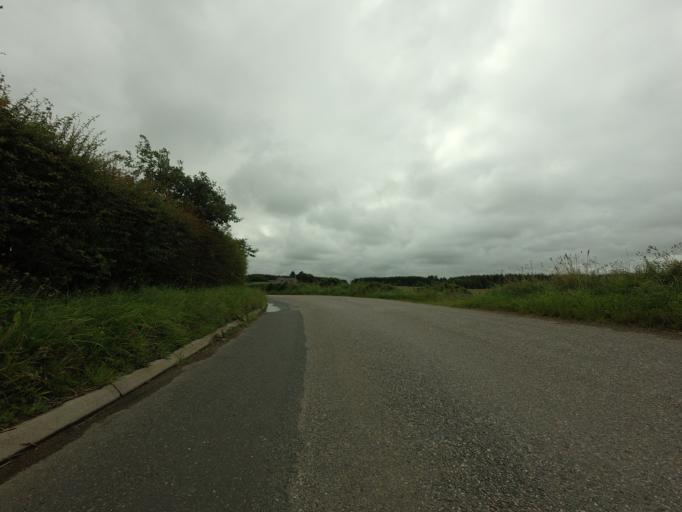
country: GB
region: Scotland
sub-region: Aberdeenshire
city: Mintlaw
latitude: 57.5263
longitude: -2.1456
